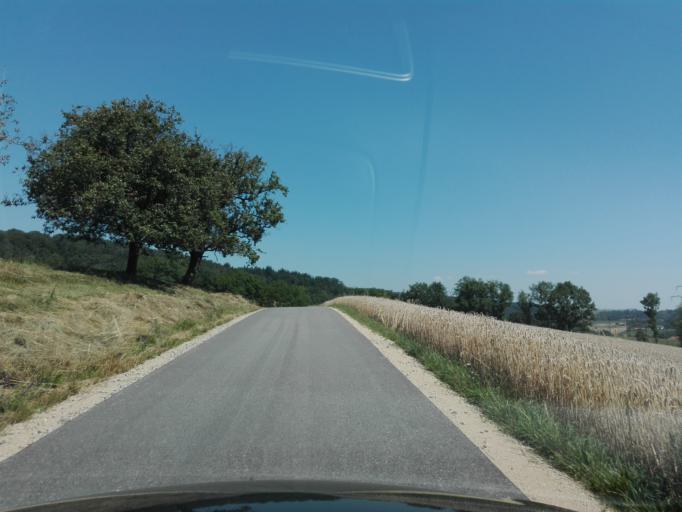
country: AT
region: Upper Austria
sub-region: Politischer Bezirk Urfahr-Umgebung
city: Steyregg
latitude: 48.3090
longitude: 14.3903
